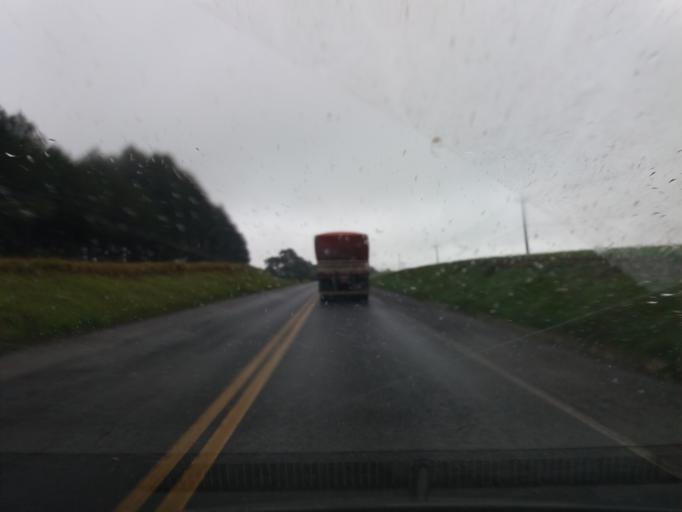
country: BR
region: Parana
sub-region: Francisco Beltrao
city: Francisco Beltrao
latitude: -26.0856
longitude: -53.2113
